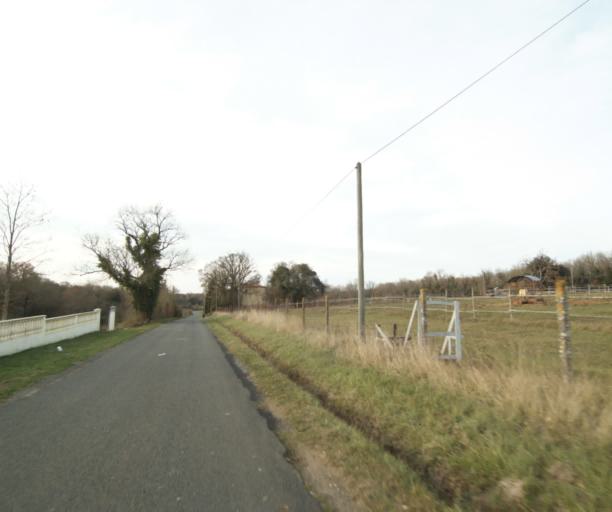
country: FR
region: Poitou-Charentes
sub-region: Departement de la Charente-Maritime
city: Saint-Hilaire-de-Villefranche
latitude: 45.8184
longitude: -0.5567
